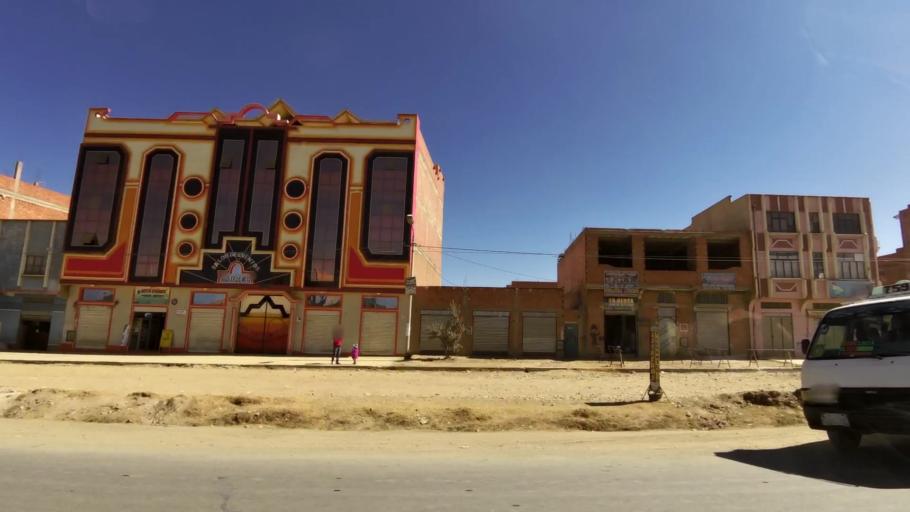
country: BO
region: La Paz
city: La Paz
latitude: -16.5647
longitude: -68.2187
